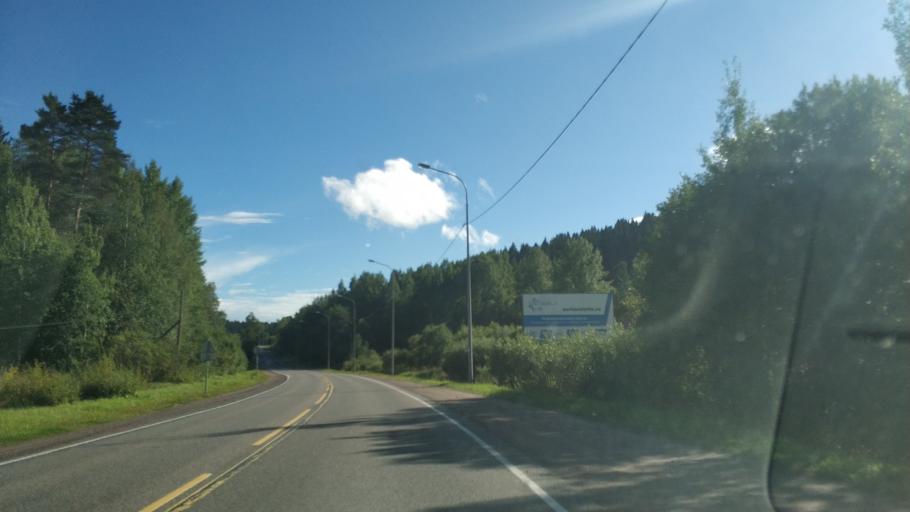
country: RU
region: Republic of Karelia
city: Sortavala
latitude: 61.6671
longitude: 30.6539
